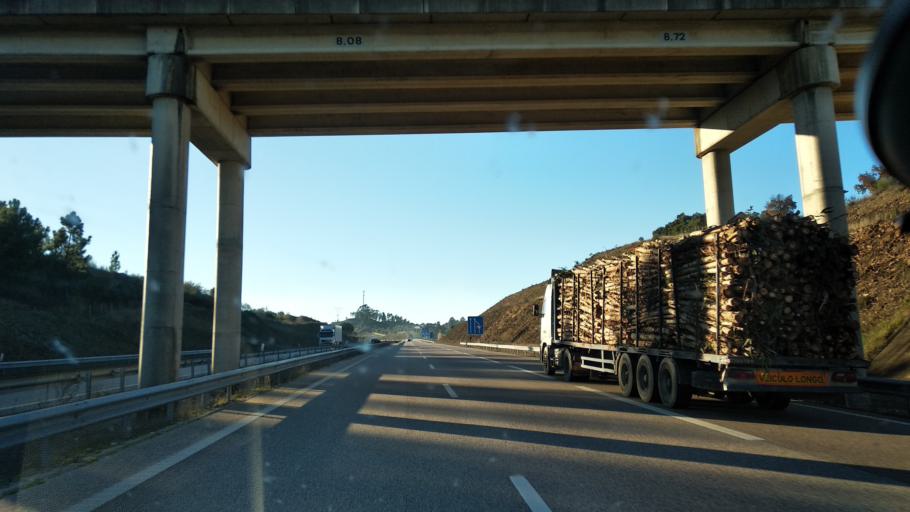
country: PT
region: Santarem
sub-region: Abrantes
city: Alferrarede
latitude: 39.4960
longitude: -8.0801
